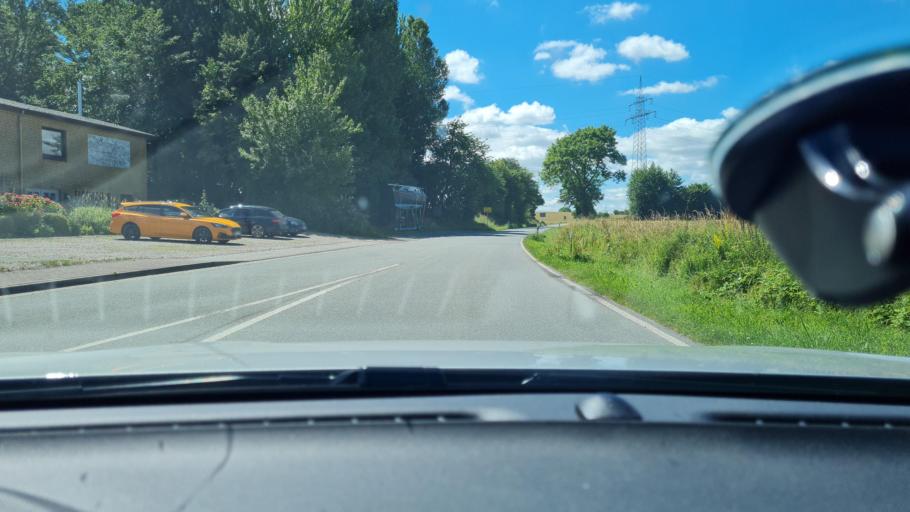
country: DE
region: Schleswig-Holstein
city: Thumby
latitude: 54.5857
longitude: 9.9101
